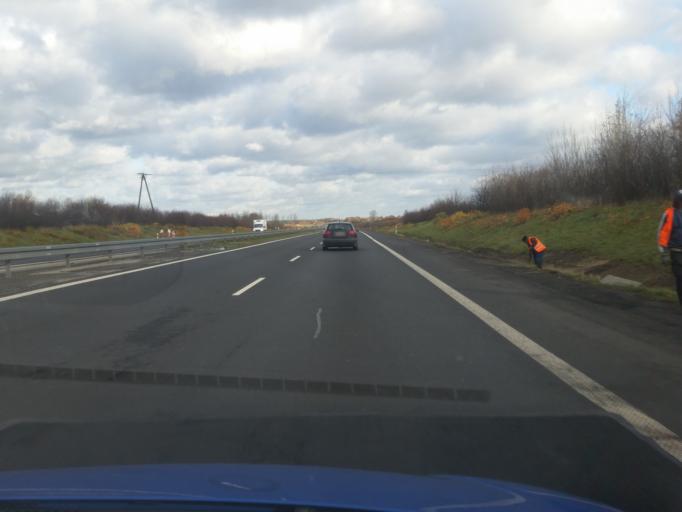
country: PL
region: Silesian Voivodeship
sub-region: Powiat czestochowski
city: Mykanow
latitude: 50.9317
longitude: 19.2301
